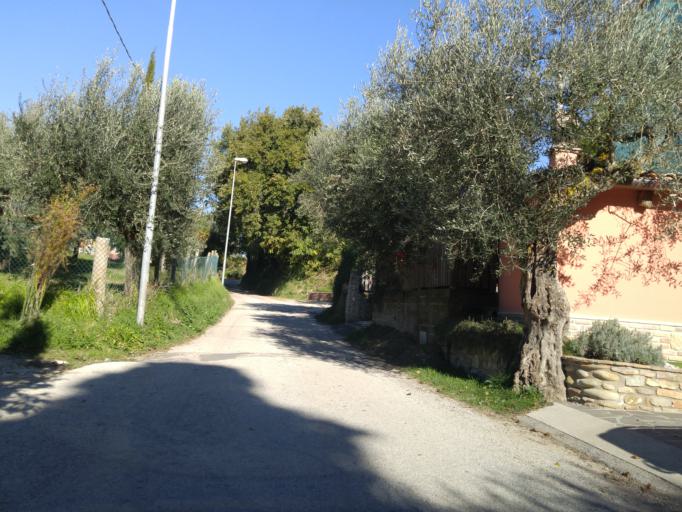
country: IT
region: The Marches
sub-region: Provincia di Pesaro e Urbino
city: Cartoceto
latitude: 43.7775
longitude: 12.8795
